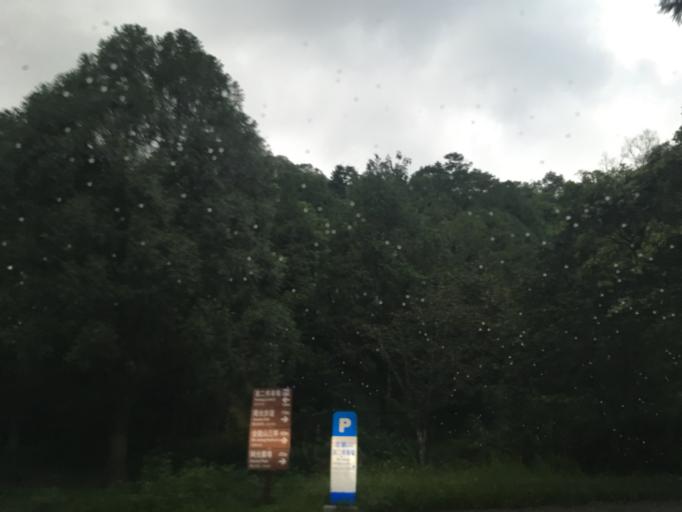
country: TW
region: Taiwan
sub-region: Nantou
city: Puli
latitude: 23.9039
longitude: 120.9076
